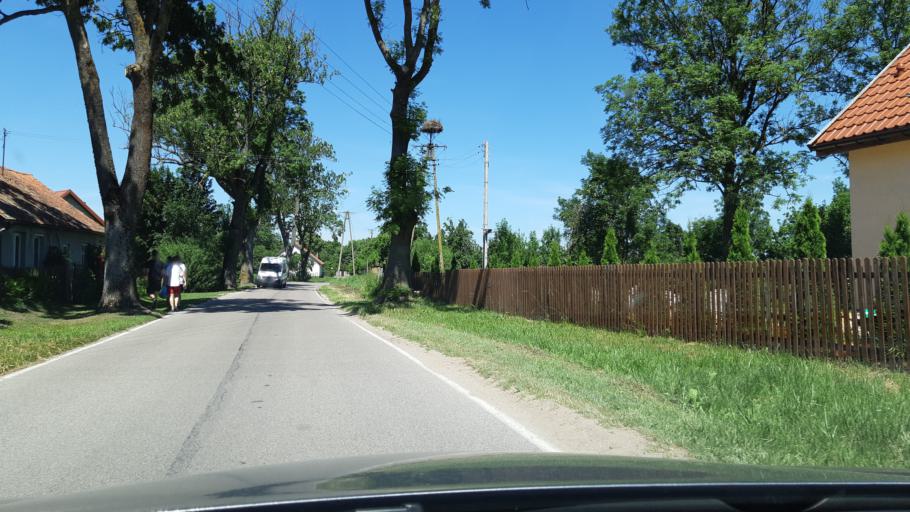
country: PL
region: Warmian-Masurian Voivodeship
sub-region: Powiat gizycki
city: Ryn
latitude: 53.8955
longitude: 21.6625
